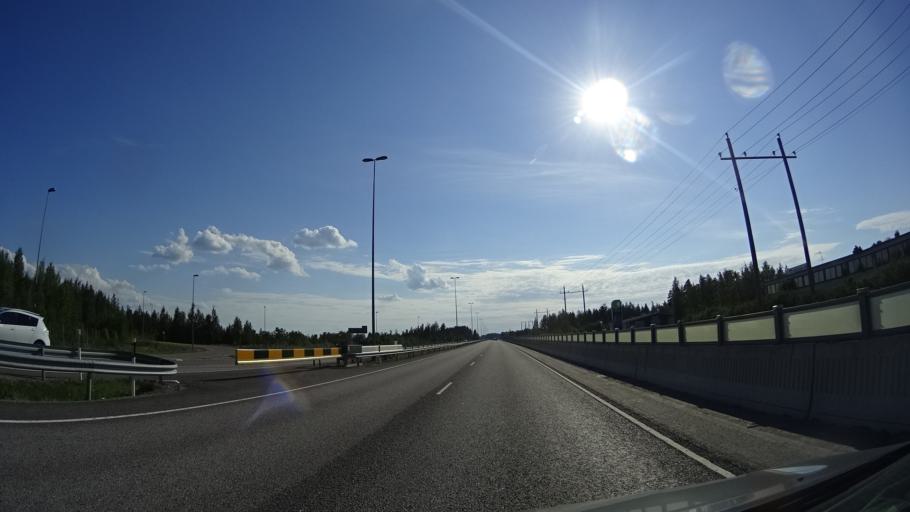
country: FI
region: South Karelia
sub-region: Imatra
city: Imatra
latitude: 61.1619
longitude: 28.6593
